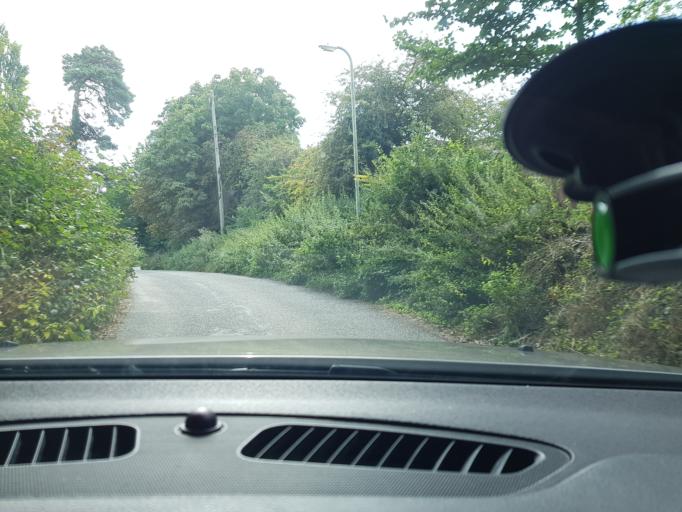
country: GB
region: England
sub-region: West Berkshire
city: Hungerford
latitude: 51.4138
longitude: -1.5269
